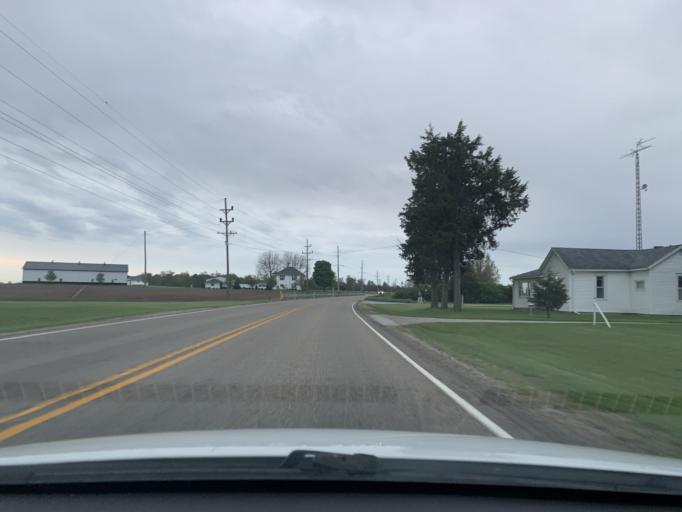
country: US
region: Indiana
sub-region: Cass County
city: Logansport
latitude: 40.8883
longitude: -86.2885
